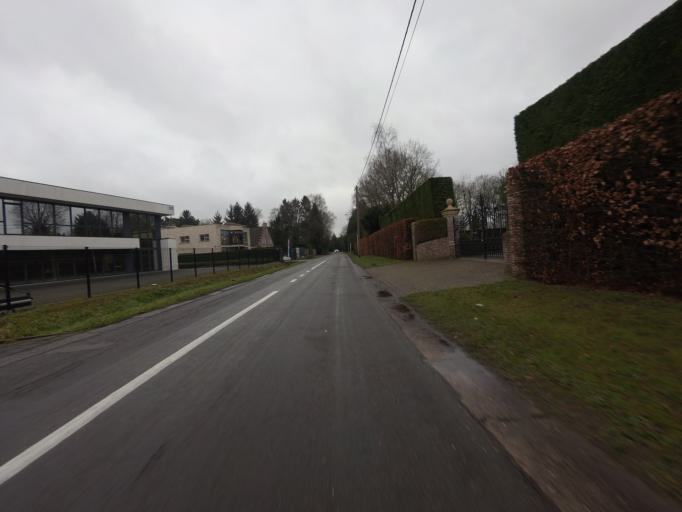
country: BE
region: Flanders
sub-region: Provincie Antwerpen
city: Sint-Katelijne-Waver
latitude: 51.0408
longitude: 4.5260
